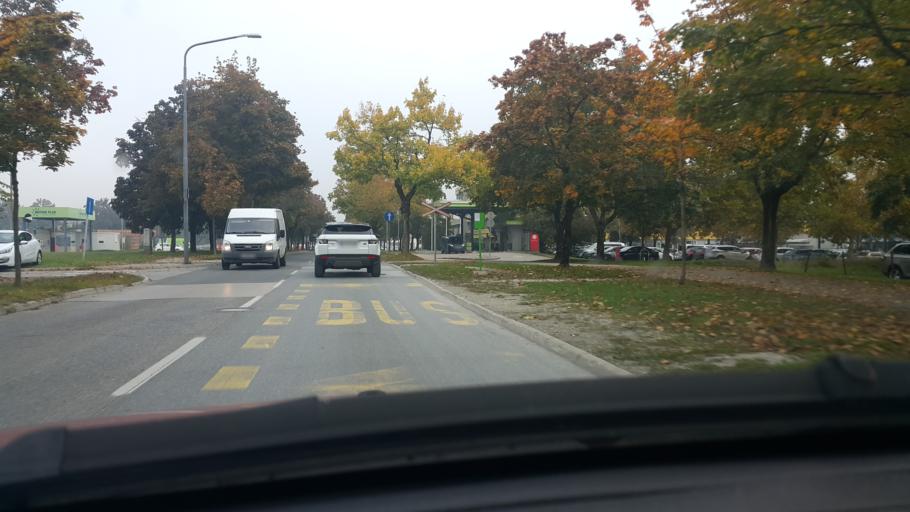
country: SI
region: Ljubljana
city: Ljubljana
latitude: 46.0801
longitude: 14.5014
